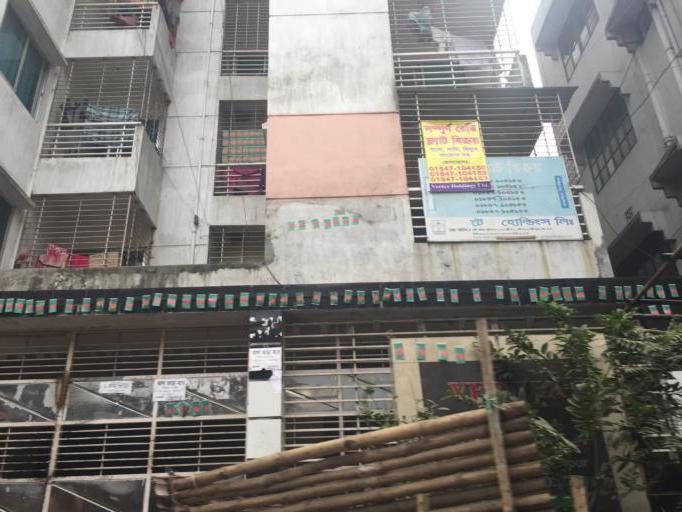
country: BD
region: Dhaka
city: Azimpur
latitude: 23.7801
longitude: 90.3606
